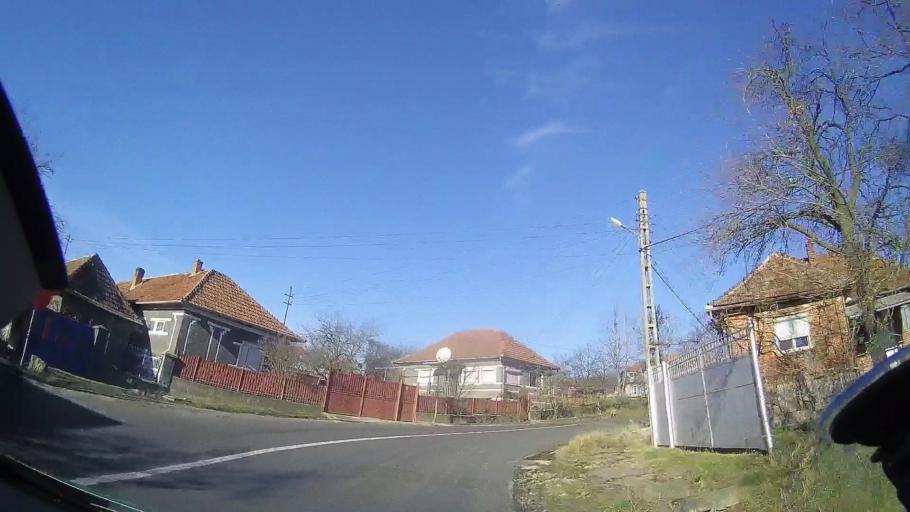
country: RO
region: Bihor
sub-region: Comuna Bratca
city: Beznea
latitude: 46.9609
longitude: 22.6164
